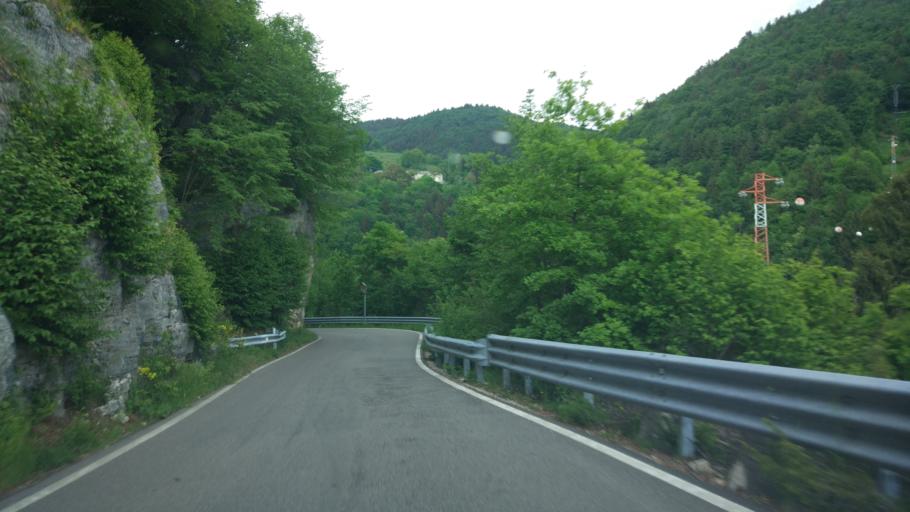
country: IT
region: Veneto
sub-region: Provincia di Verona
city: Erbezzo
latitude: 45.6517
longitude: 11.0140
